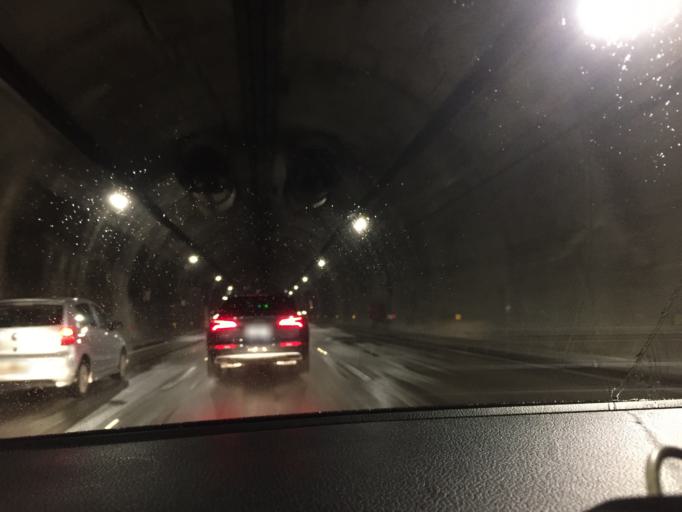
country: BR
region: Sao Paulo
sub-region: Cubatao
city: Cubatao
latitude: -23.8832
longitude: -46.4939
